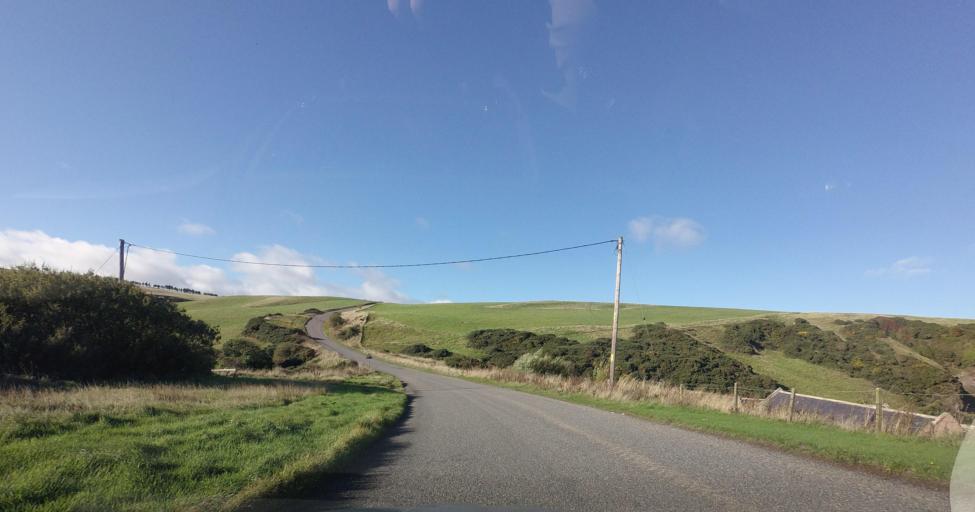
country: GB
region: Scotland
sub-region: Aberdeenshire
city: Rosehearty
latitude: 57.6802
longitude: -2.2707
